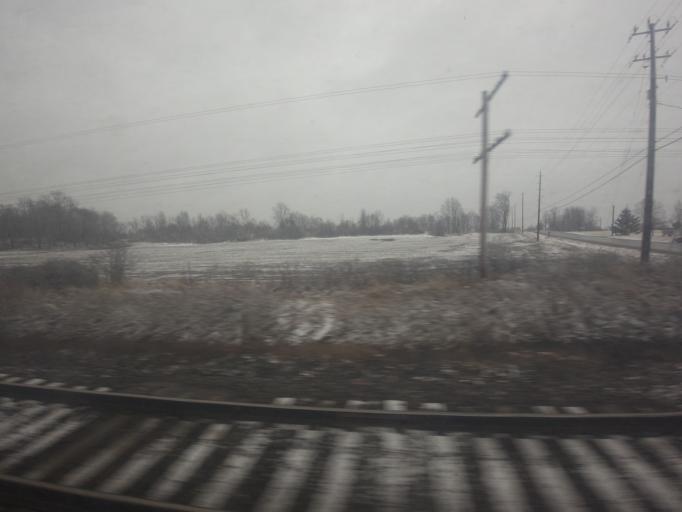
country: US
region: New York
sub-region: Jefferson County
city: Alexandria Bay
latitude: 44.4917
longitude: -75.8721
